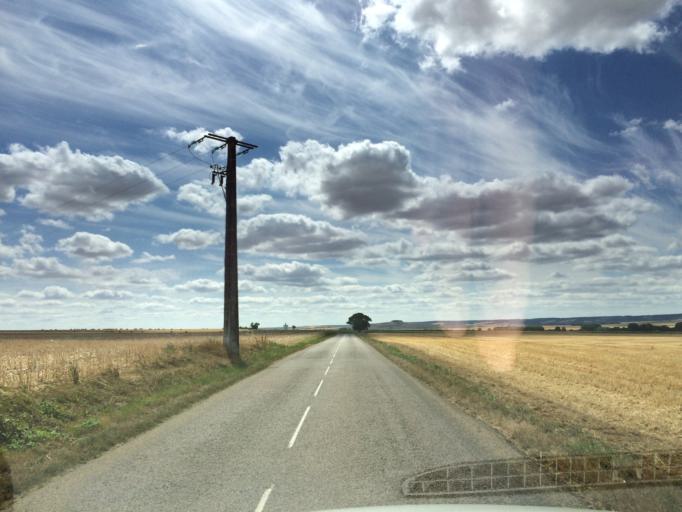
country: FR
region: Bourgogne
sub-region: Departement de l'Yonne
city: Laroche-Saint-Cydroine
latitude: 47.9376
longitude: 3.4655
